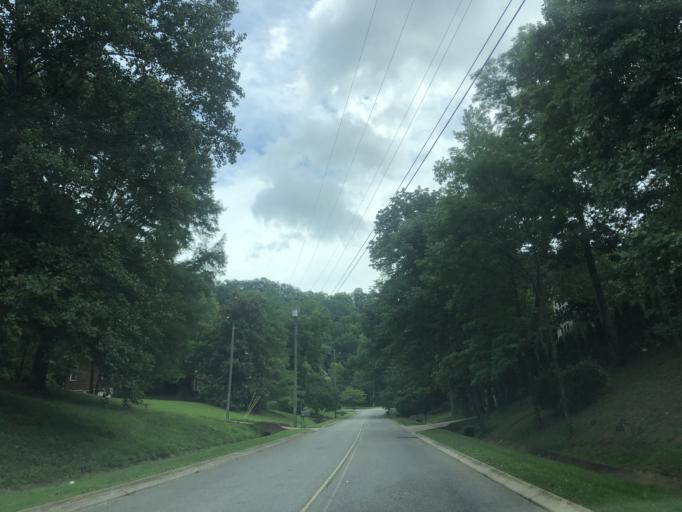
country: US
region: Tennessee
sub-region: Davidson County
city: Oak Hill
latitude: 36.0729
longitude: -86.8070
